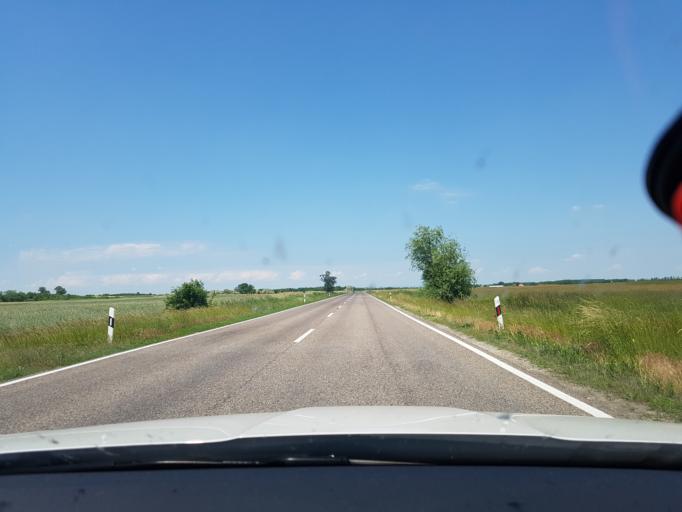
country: HU
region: Hajdu-Bihar
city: Egyek
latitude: 47.5746
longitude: 20.8575
